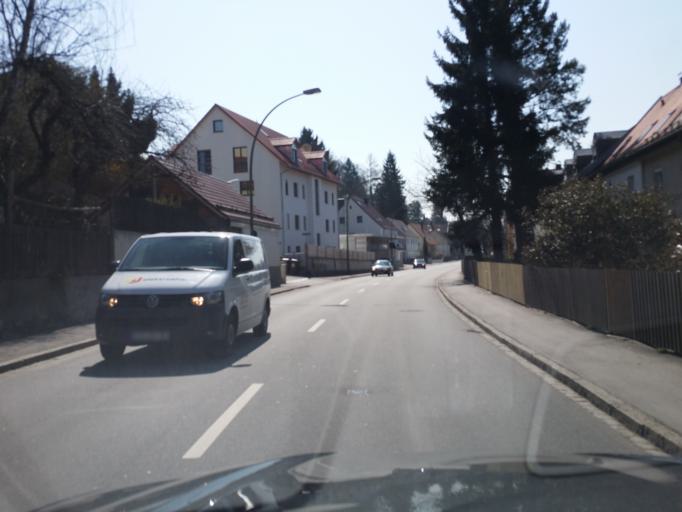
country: DE
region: Bavaria
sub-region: Lower Bavaria
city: Landshut
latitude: 48.5186
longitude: 12.1513
